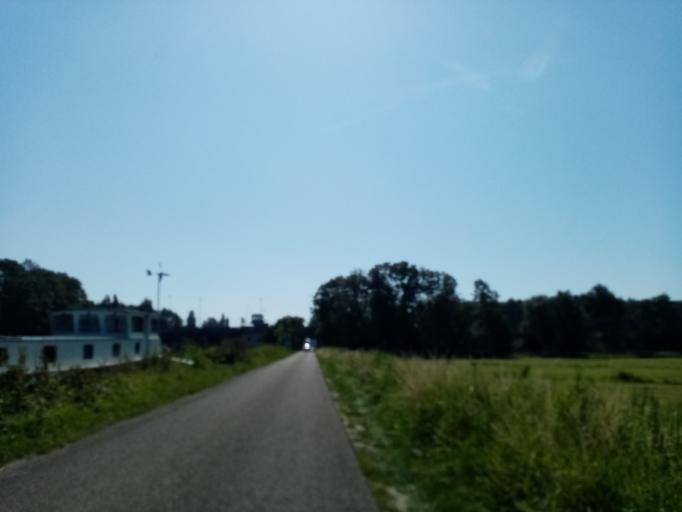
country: NL
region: South Holland
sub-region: Gemeente Teylingen
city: Sassenheim
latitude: 52.2253
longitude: 4.5510
